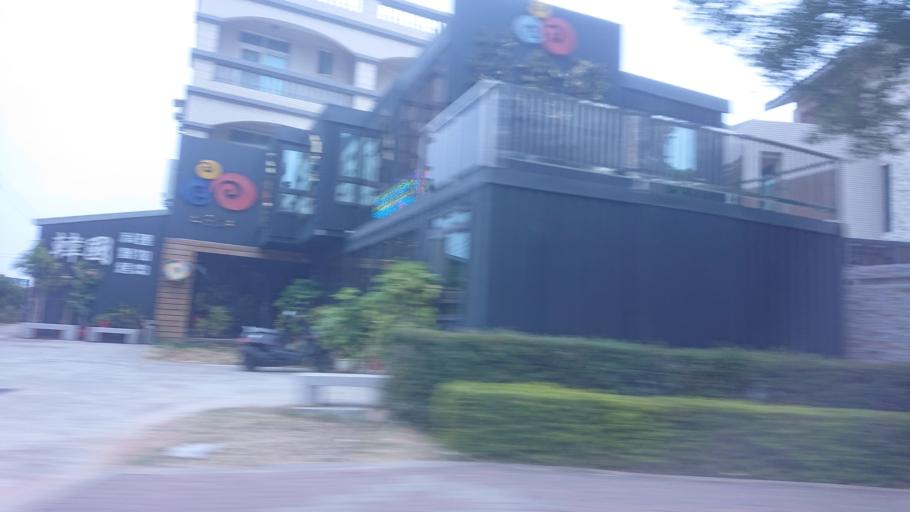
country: TW
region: Fukien
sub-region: Kinmen
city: Jincheng
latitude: 24.4406
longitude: 118.3119
